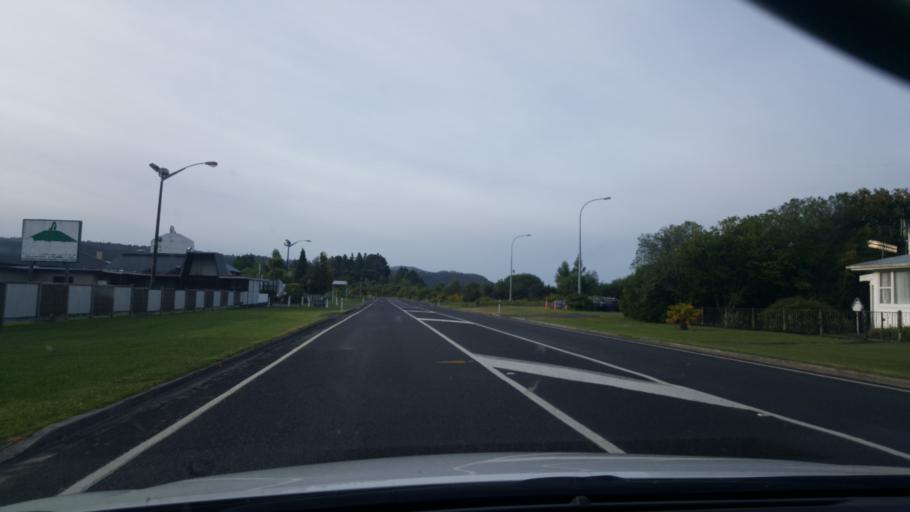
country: NZ
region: Waikato
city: Turangi
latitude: -38.9641
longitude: 175.7661
